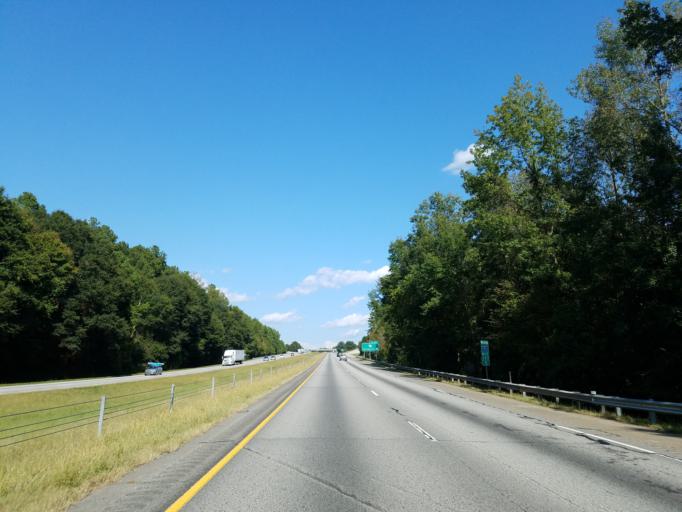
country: US
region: Georgia
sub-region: Franklin County
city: Carnesville
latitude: 34.3719
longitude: -83.2676
